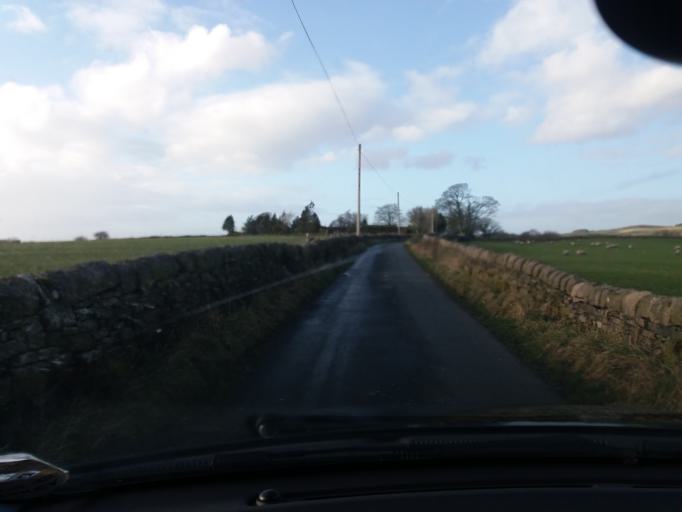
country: GB
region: England
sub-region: Lancashire
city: Adlington
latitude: 53.6347
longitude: -2.5814
